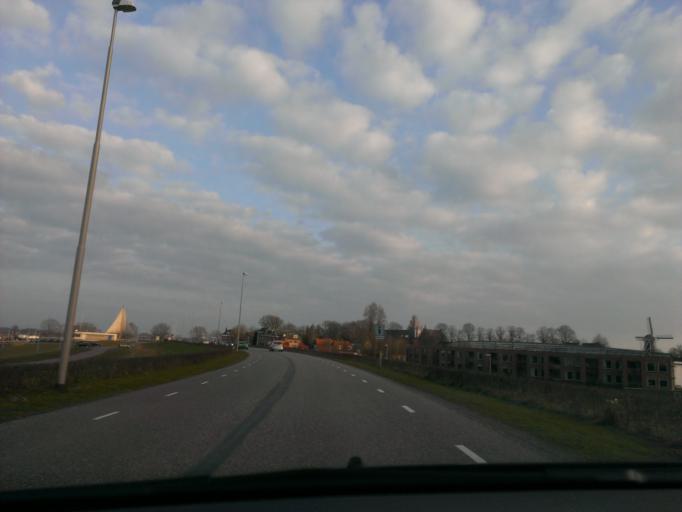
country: NL
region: Gelderland
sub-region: Gemeente Hattem
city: Hattem
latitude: 52.4782
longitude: 6.0653
